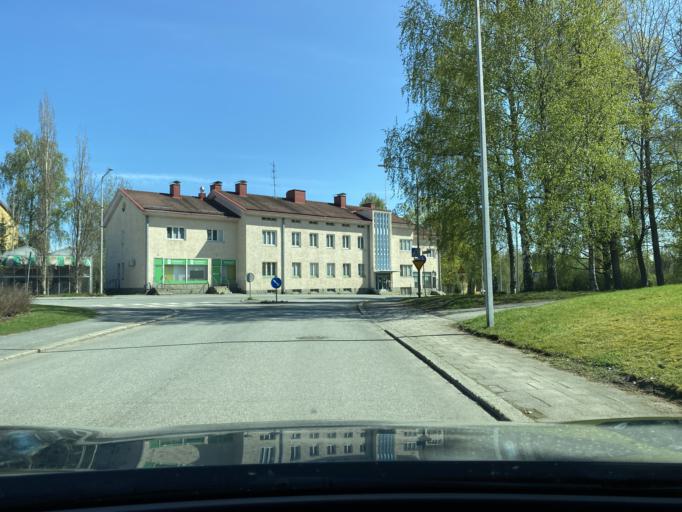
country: FI
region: Pirkanmaa
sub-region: Lounais-Pirkanmaa
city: Vammala
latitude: 61.3475
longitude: 22.8990
